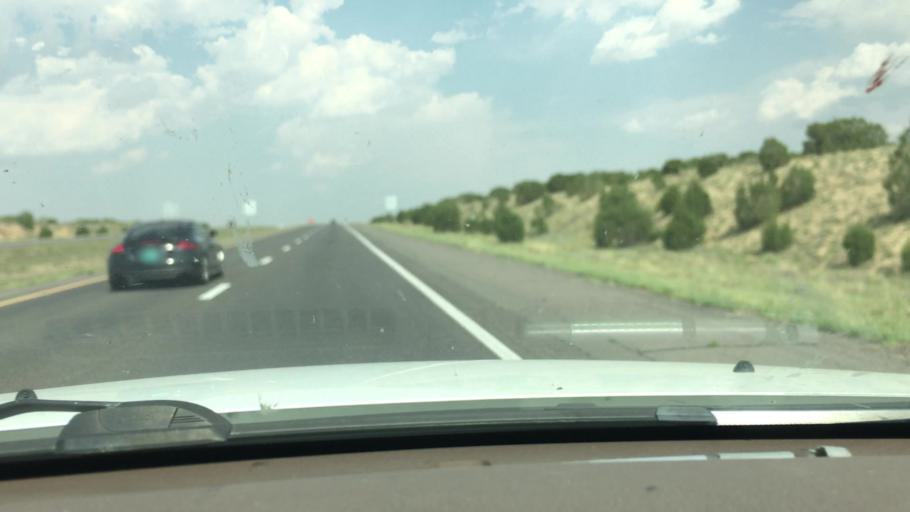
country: US
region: New Mexico
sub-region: Cibola County
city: Skyline-Ganipa
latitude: 35.0757
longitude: -107.6366
